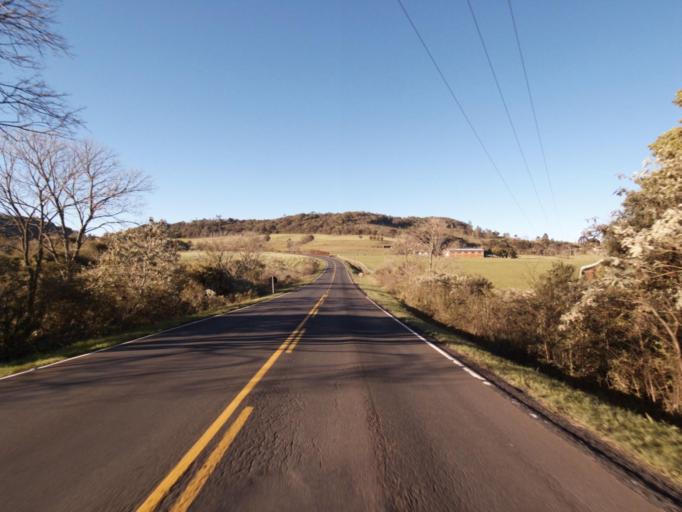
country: AR
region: Misiones
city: Bernardo de Irigoyen
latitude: -26.3523
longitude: -53.5442
